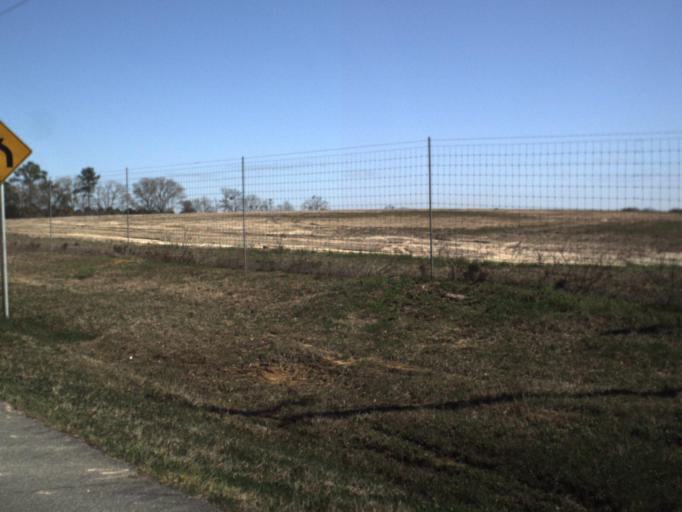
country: US
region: Florida
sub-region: Jackson County
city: Sneads
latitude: 30.6921
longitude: -85.0214
